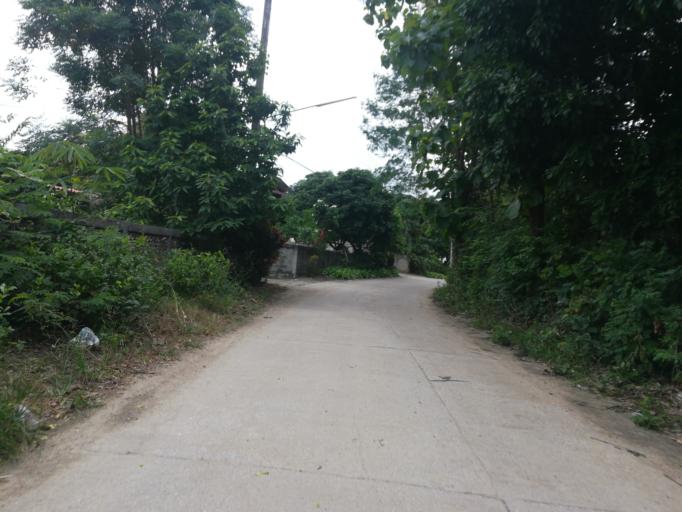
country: TH
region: Chiang Mai
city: Chom Thong
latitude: 18.4043
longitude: 98.6510
